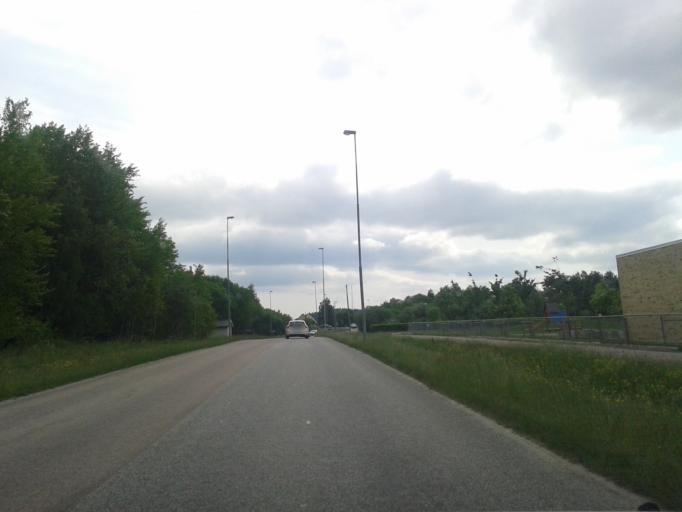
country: SE
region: Vaestra Goetaland
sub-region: Kungalvs Kommun
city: Kungalv
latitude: 57.8890
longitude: 11.9682
